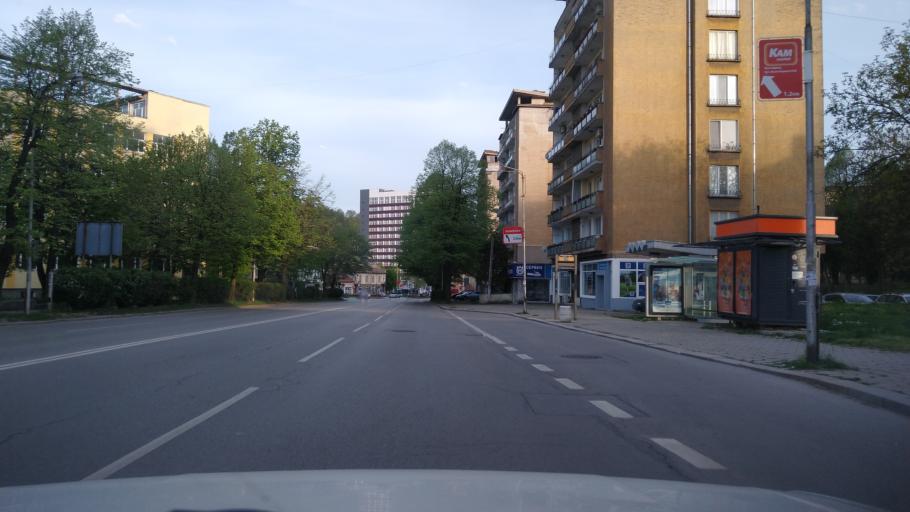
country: BG
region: Gabrovo
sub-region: Obshtina Gabrovo
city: Gabrovo
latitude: 42.8784
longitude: 25.3155
